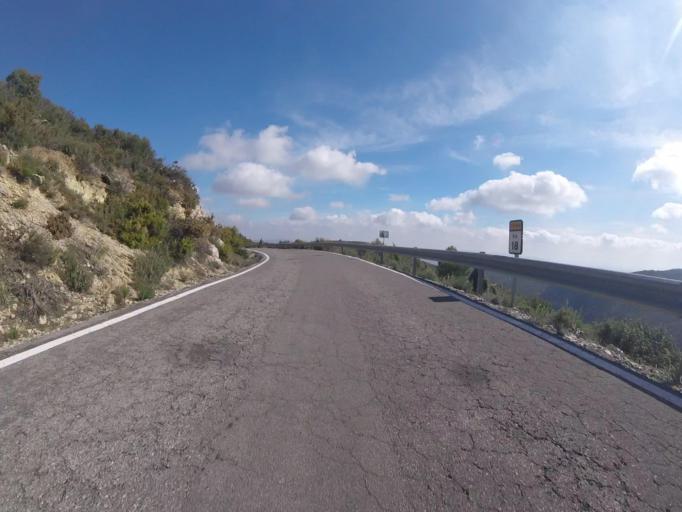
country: ES
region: Valencia
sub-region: Provincia de Castello
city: Albocasser
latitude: 40.3378
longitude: 0.0459
